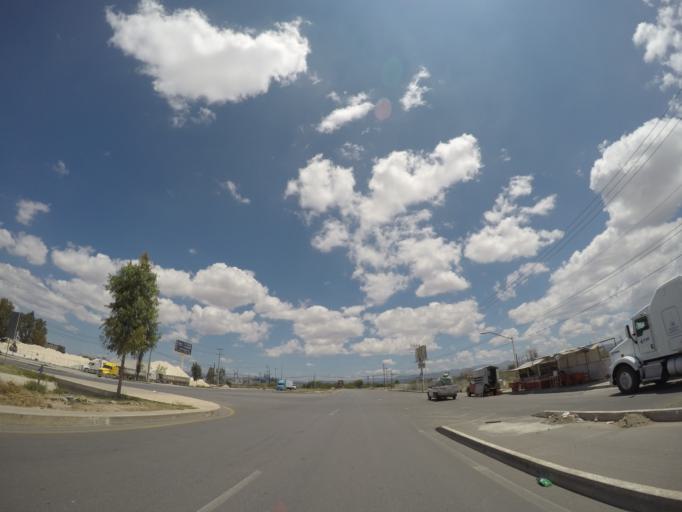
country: MX
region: San Luis Potosi
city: La Pila
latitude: 22.0520
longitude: -100.8634
